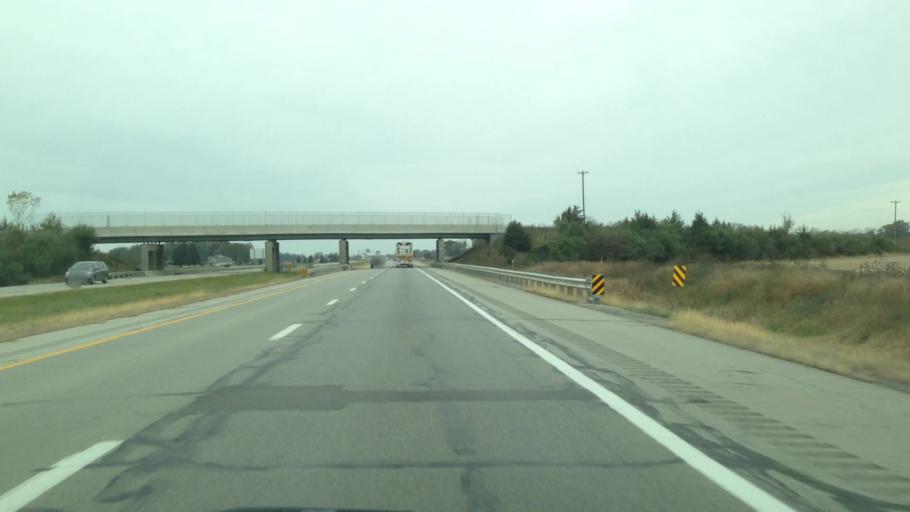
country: US
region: Ohio
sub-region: Fulton County
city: Burlington
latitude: 41.5900
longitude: -84.3506
